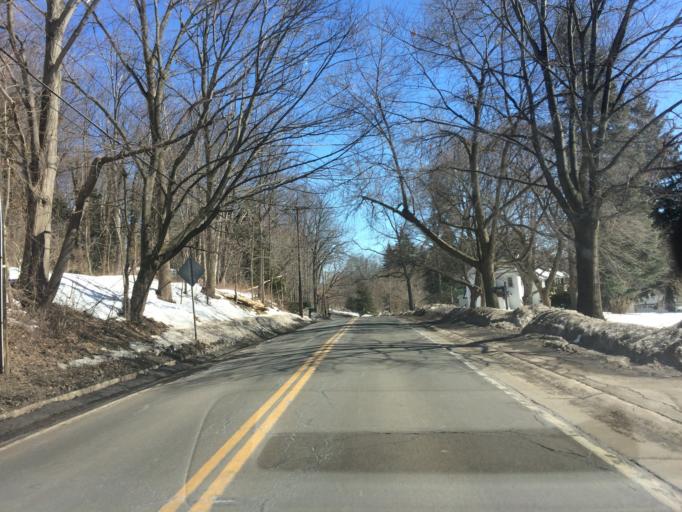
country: US
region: New York
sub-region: Monroe County
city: Rochester
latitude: 43.1308
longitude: -77.5949
